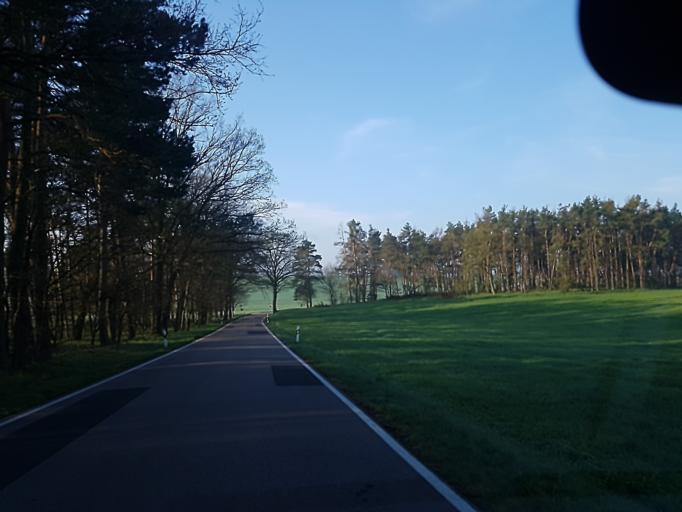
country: DE
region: Saxony
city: Cavertitz
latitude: 51.4093
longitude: 13.1395
